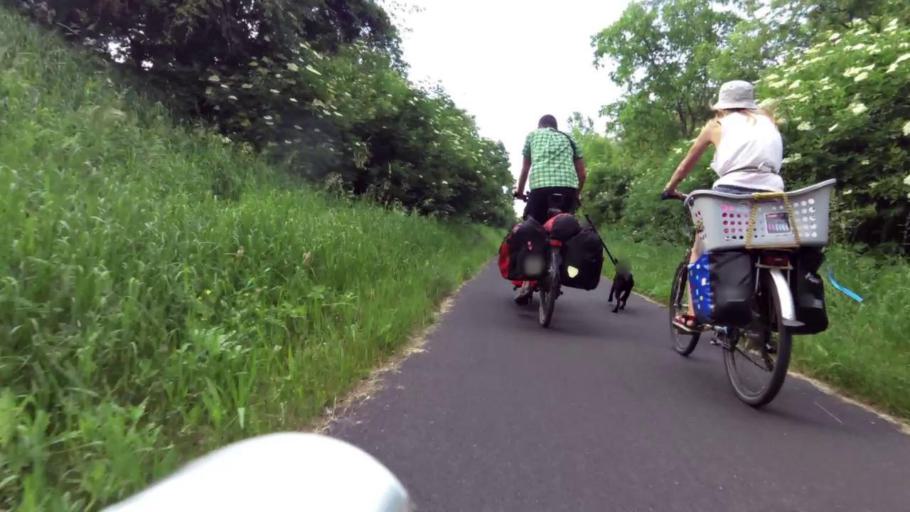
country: PL
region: Kujawsko-Pomorskie
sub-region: Powiat torunski
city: Lubianka
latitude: 53.0930
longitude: 18.5326
